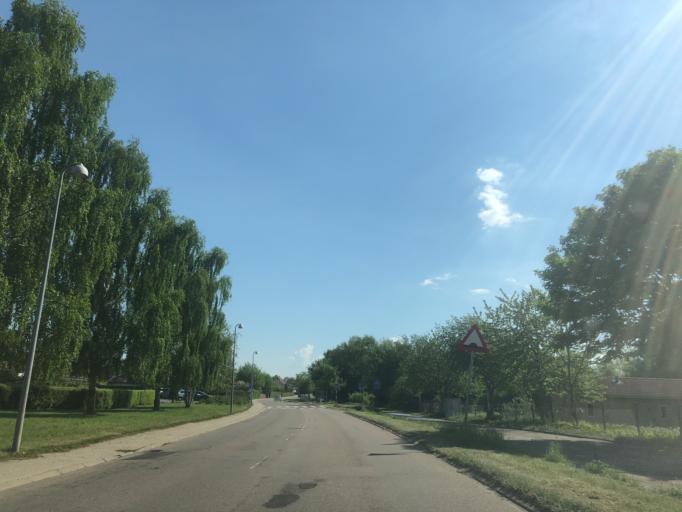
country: DK
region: Zealand
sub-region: Solrod Kommune
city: Havdrup
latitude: 55.5736
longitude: 12.0908
